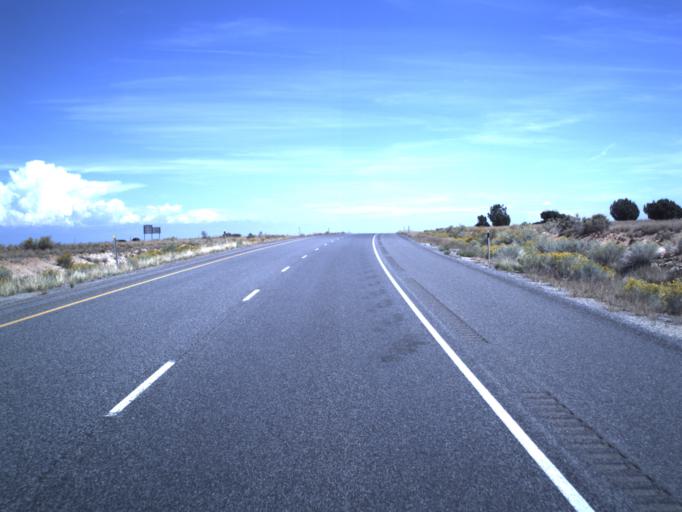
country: US
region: Utah
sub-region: Emery County
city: Castle Dale
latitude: 38.8907
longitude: -110.6409
